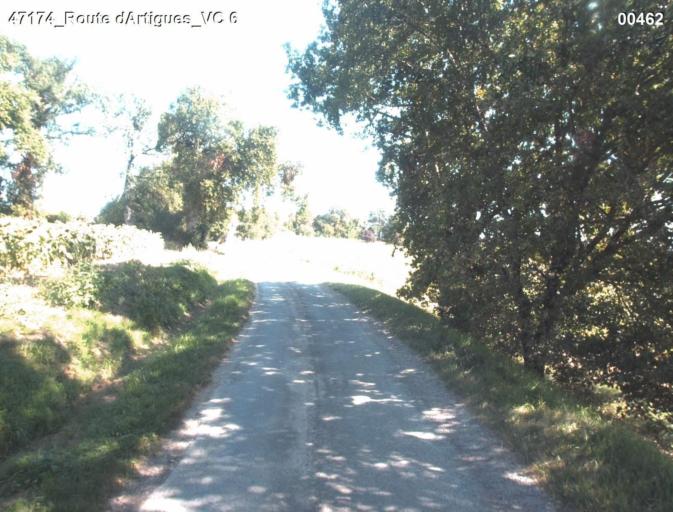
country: FR
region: Midi-Pyrenees
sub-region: Departement du Gers
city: Condom
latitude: 44.0124
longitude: 0.3299
